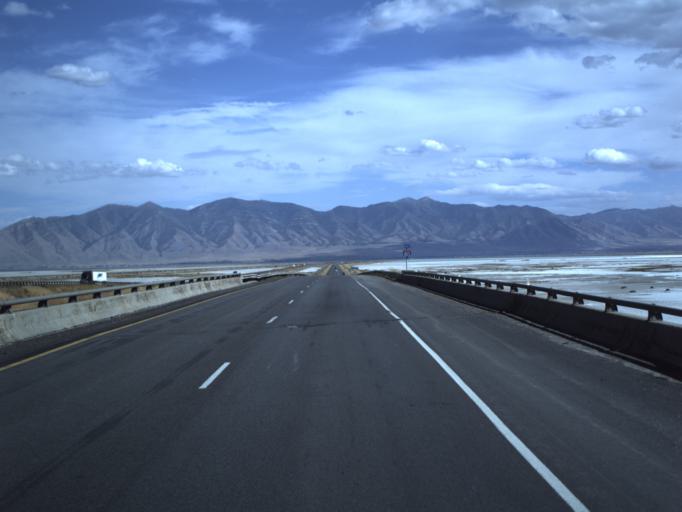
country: US
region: Utah
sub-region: Tooele County
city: Grantsville
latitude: 40.6839
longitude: -112.4408
